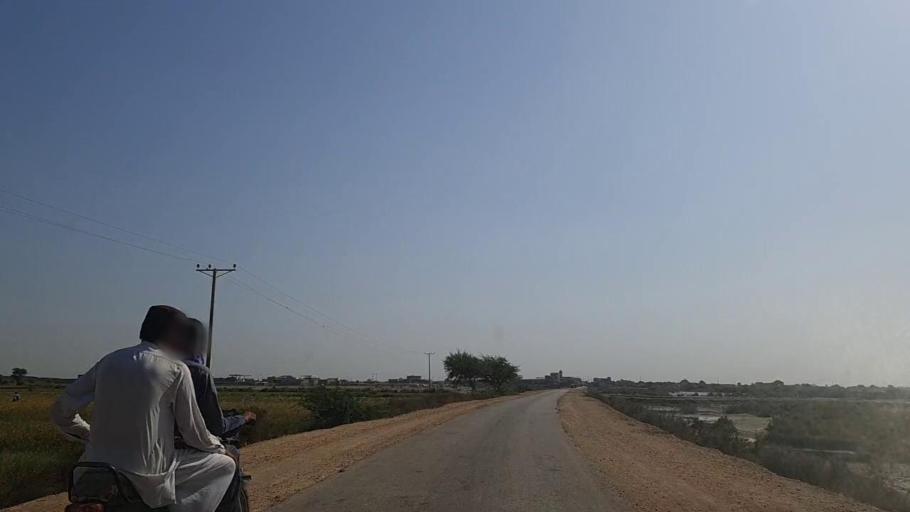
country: PK
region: Sindh
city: Mirpur Batoro
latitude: 24.6240
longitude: 68.2946
